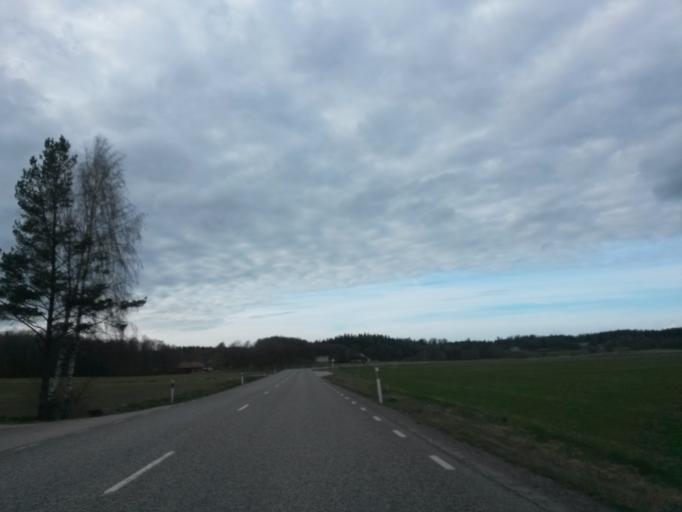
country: SE
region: Vaestra Goetaland
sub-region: Vargarda Kommun
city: Jonstorp
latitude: 58.0277
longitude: 12.6334
